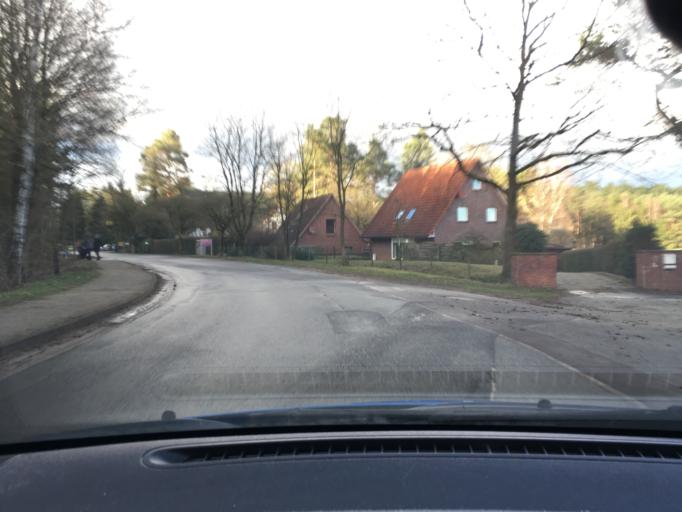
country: DE
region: Lower Saxony
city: Asendorf
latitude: 53.3016
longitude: 9.9864
